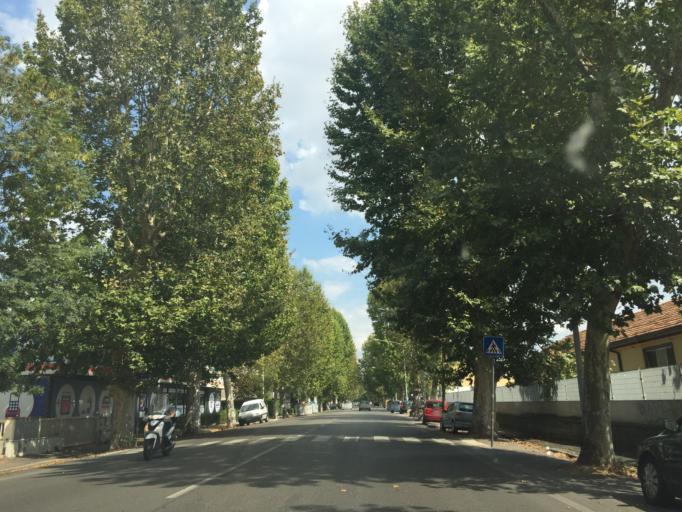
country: IT
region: Tuscany
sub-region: Province of Florence
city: Mantignano-Ugnano
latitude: 43.7941
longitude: 11.1882
